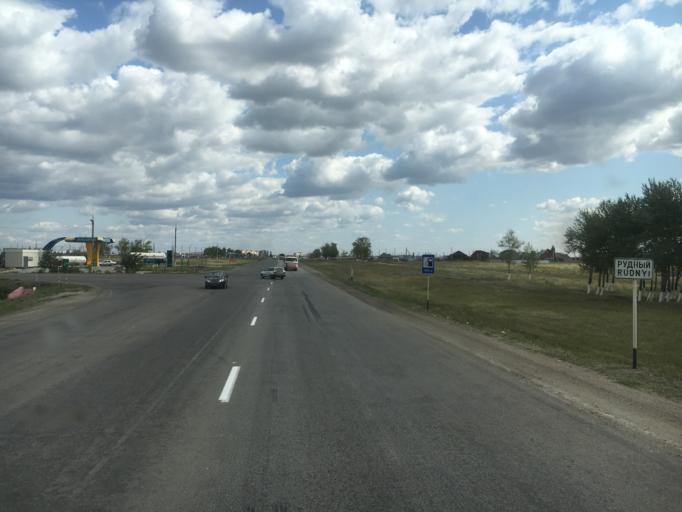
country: KZ
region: Qostanay
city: Rudnyy
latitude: 52.9494
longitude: 63.0595
